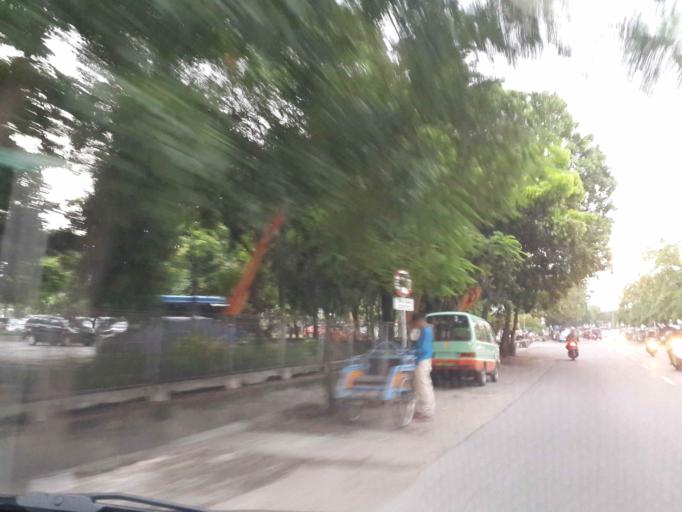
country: ID
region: East Java
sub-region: Kota Surabaya
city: Surabaya
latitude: -7.2495
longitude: 112.7313
